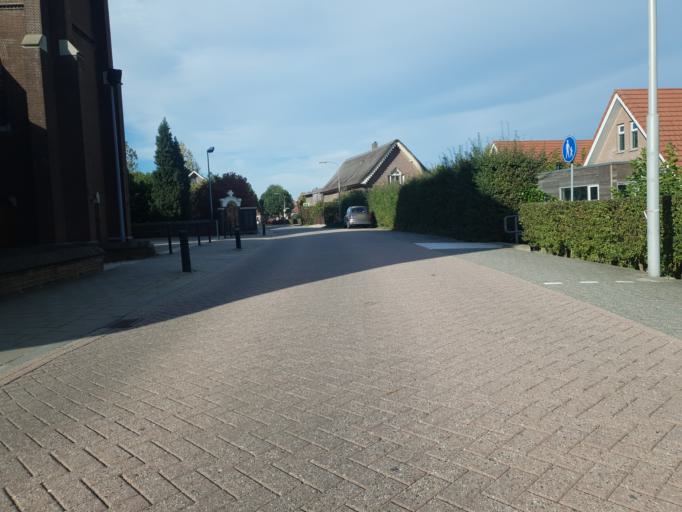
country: NL
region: Gelderland
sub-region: Gemeente Groesbeek
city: Berg en Dal
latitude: 51.8534
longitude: 5.9394
